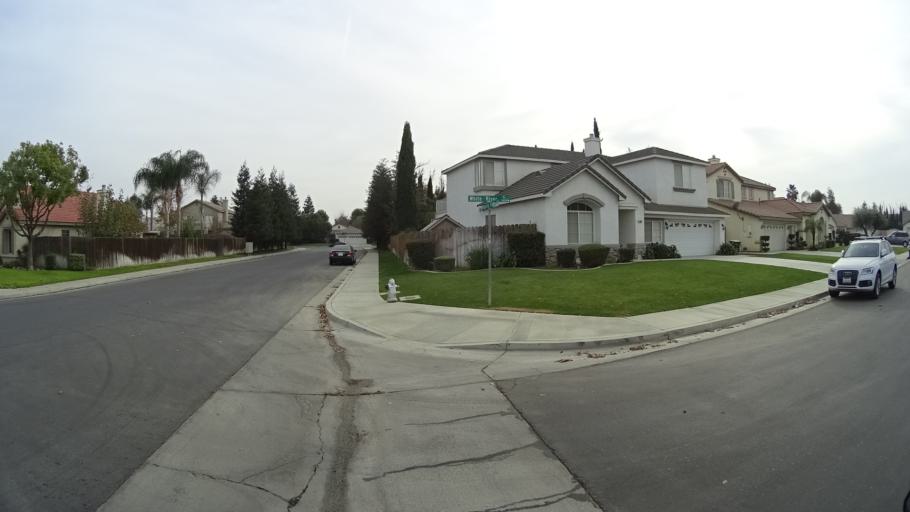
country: US
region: California
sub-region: Kern County
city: Rosedale
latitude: 35.3454
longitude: -119.1312
